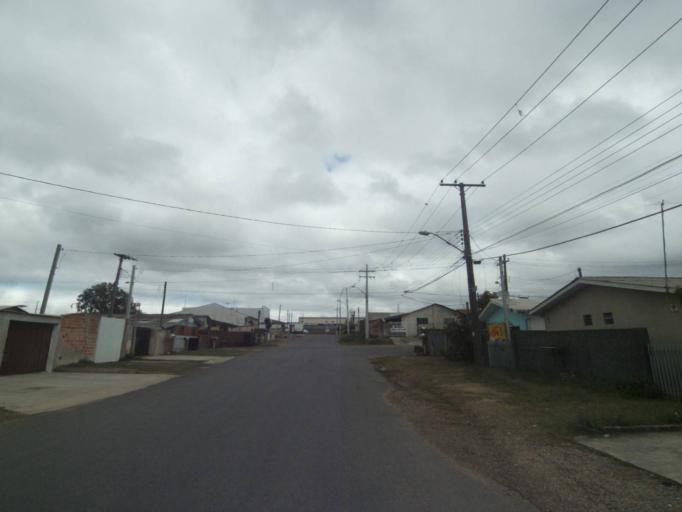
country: BR
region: Parana
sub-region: Sao Jose Dos Pinhais
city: Sao Jose dos Pinhais
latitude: -25.5432
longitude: -49.2997
